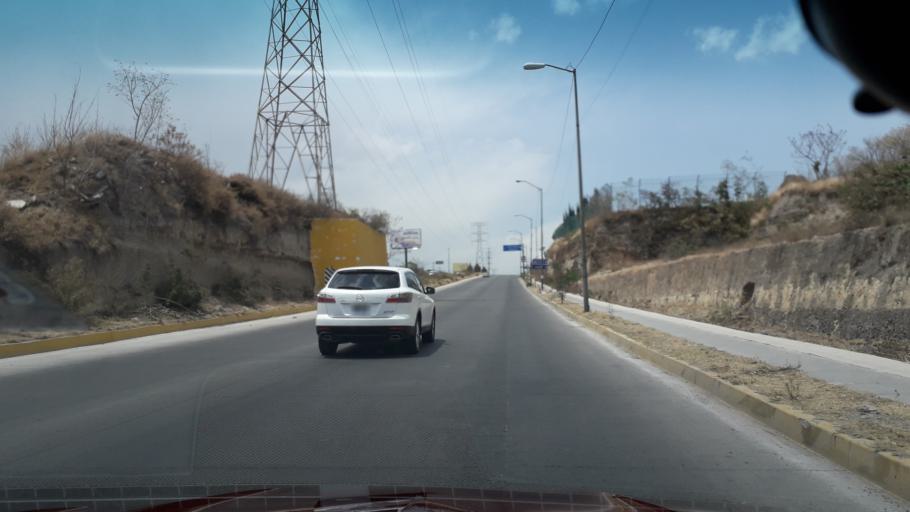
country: MX
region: Puebla
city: Tlazcalancingo
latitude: 19.0148
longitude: -98.2471
